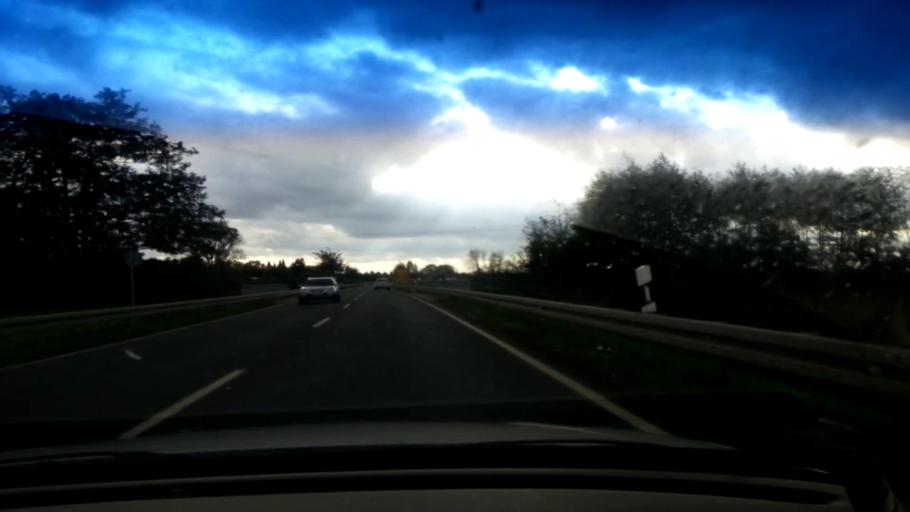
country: DE
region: Bavaria
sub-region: Upper Franconia
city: Memmelsdorf
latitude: 49.9337
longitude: 10.9497
